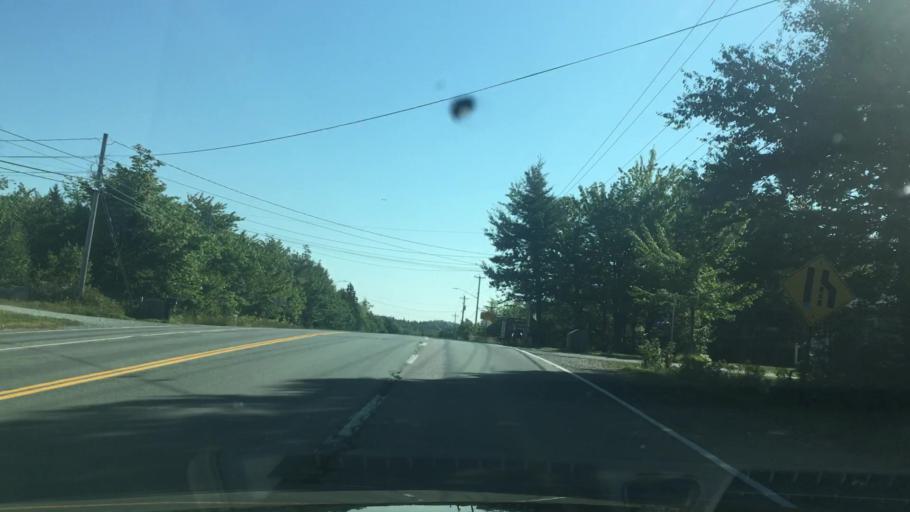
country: CA
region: Nova Scotia
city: Cole Harbour
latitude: 44.7781
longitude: -63.0891
